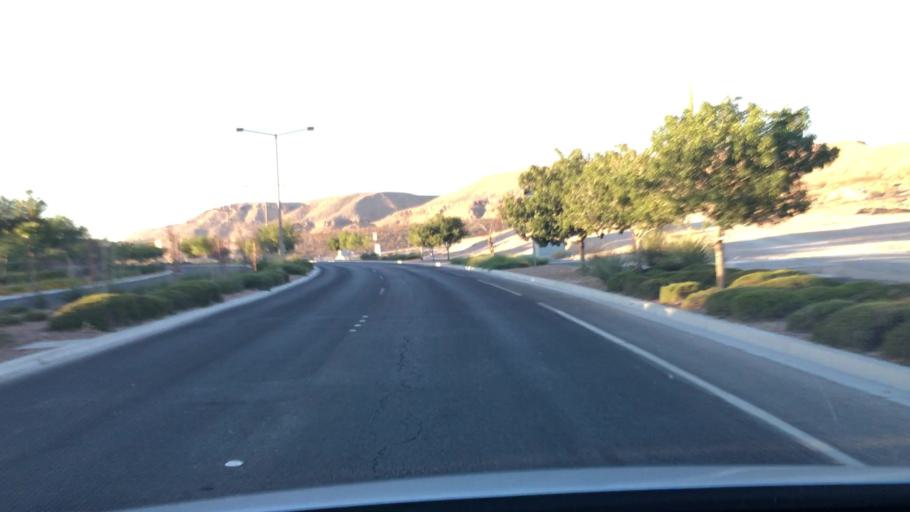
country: US
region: Nevada
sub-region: Clark County
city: Summerlin South
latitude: 36.1043
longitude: -115.3277
